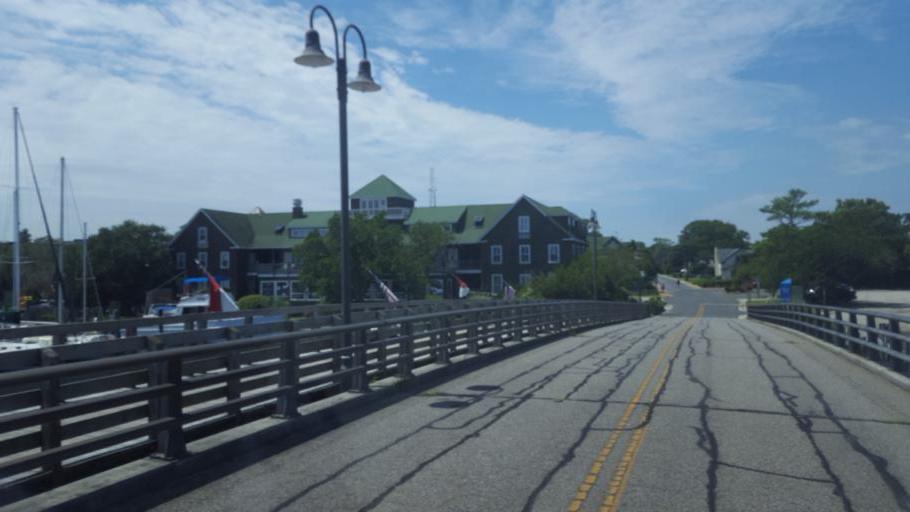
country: US
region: North Carolina
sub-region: Dare County
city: Manteo
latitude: 35.9110
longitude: -75.6687
